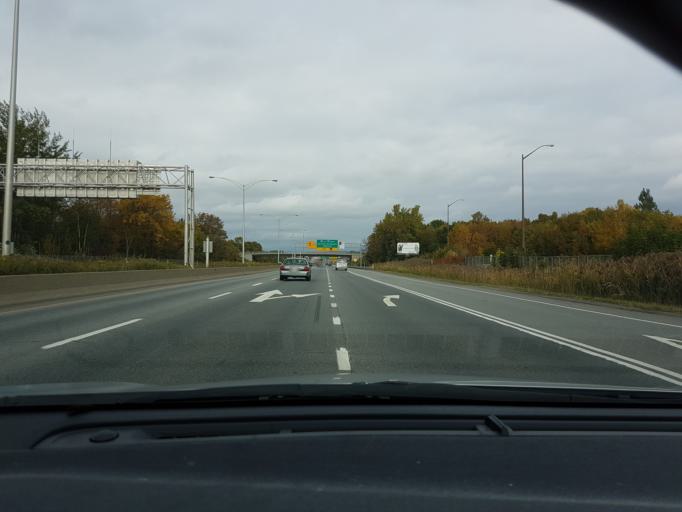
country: CA
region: Quebec
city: L'Ancienne-Lorette
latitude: 46.8170
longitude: -71.2914
